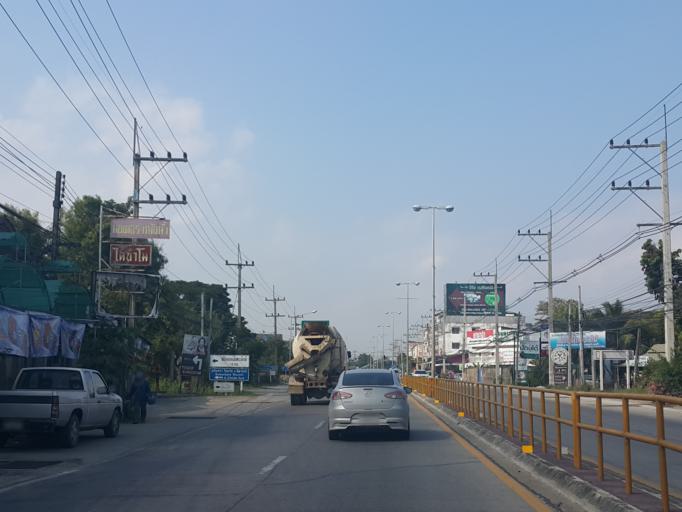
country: TH
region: Chiang Mai
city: San Sai
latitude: 18.9207
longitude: 98.9418
